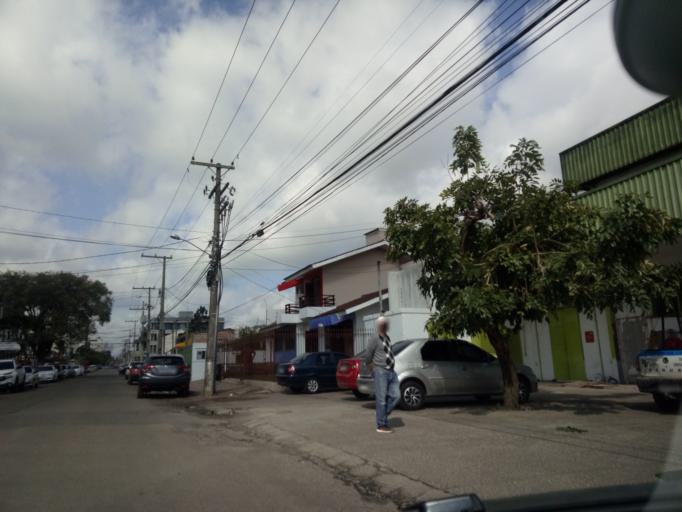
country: BR
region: Rio Grande do Sul
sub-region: Santa Maria
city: Santa Maria
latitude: -29.7018
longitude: -53.7225
